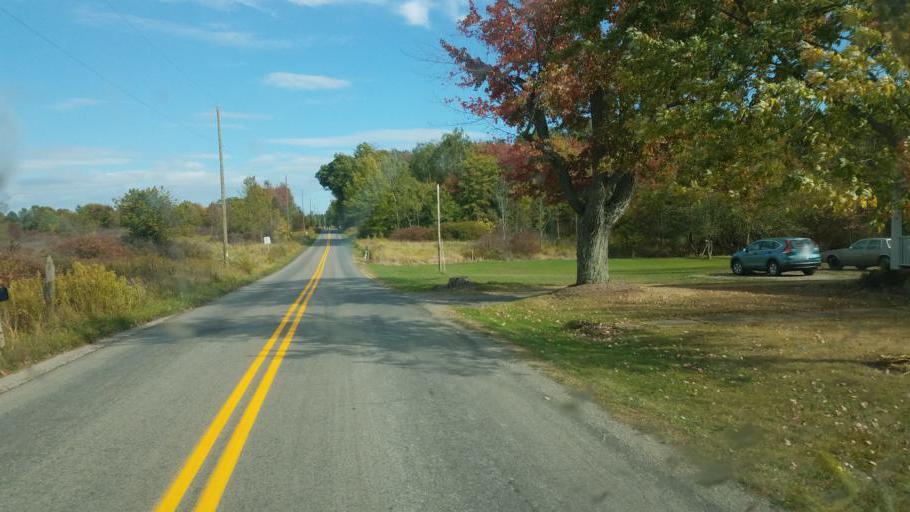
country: US
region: Pennsylvania
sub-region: Mercer County
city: Mercer
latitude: 41.3496
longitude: -80.2313
